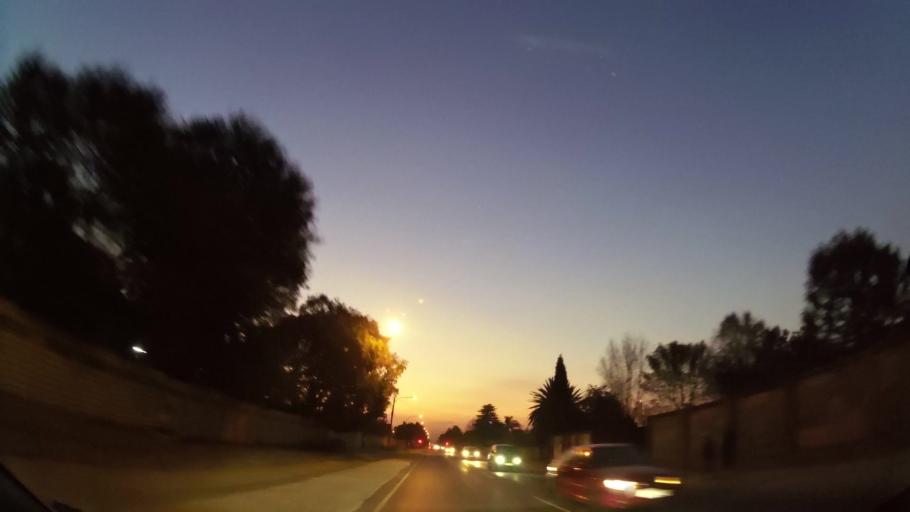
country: ZA
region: Gauteng
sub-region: Ekurhuleni Metropolitan Municipality
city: Benoni
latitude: -26.0922
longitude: 28.3042
